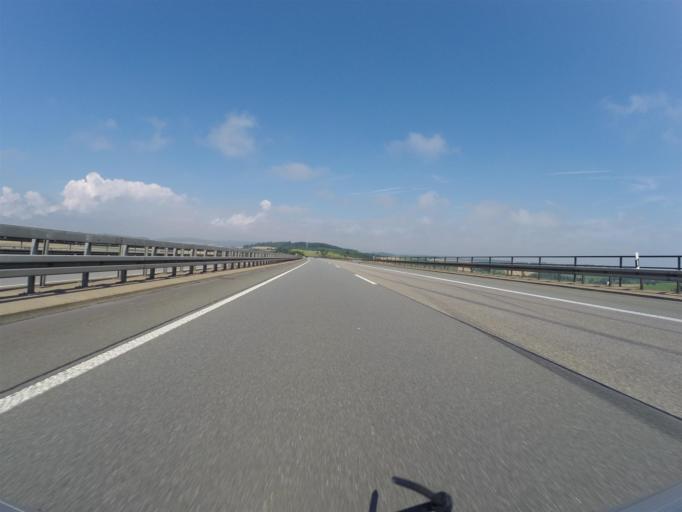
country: DE
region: North Rhine-Westphalia
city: Warburg
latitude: 51.4623
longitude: 9.1208
